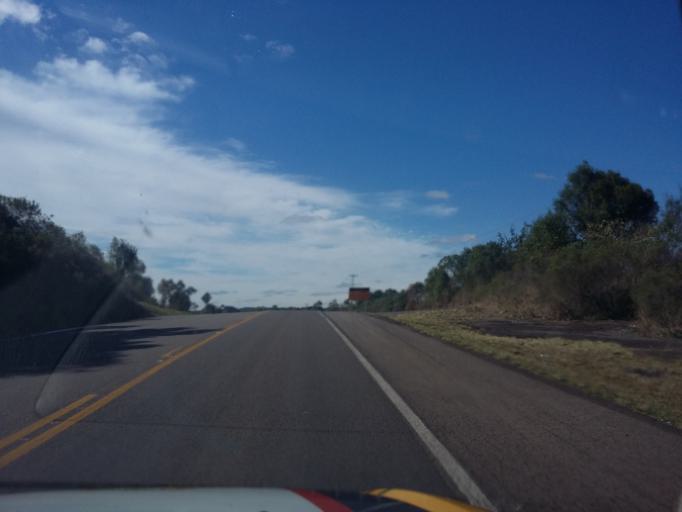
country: BR
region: Rio Grande do Sul
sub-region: Vacaria
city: Vacaria
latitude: -28.5958
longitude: -51.0323
